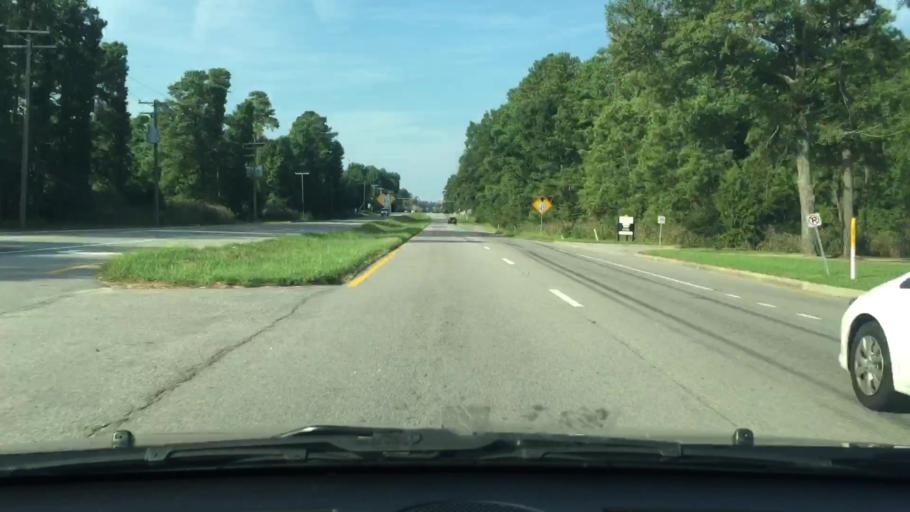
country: US
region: Virginia
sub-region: Isle of Wight County
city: Carrollton
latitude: 36.9611
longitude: -76.5201
